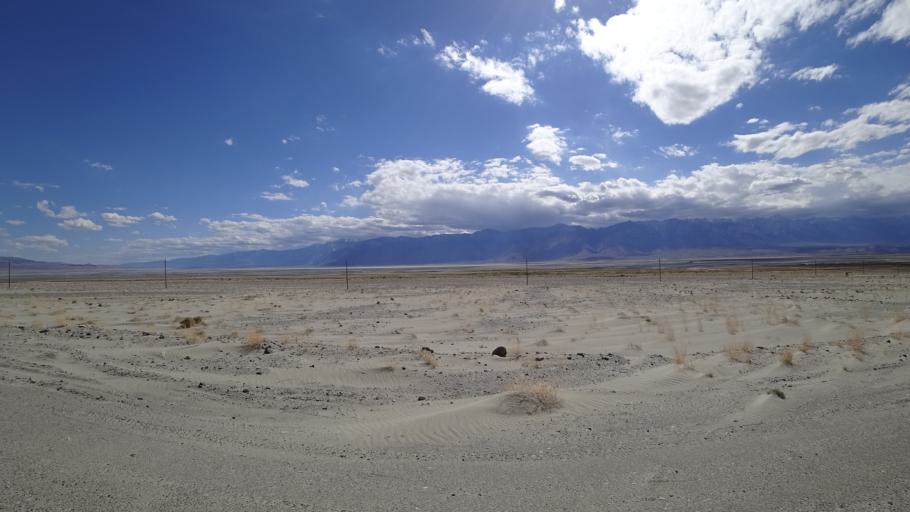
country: US
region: California
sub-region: Inyo County
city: Lone Pine
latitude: 36.5137
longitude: -117.8962
